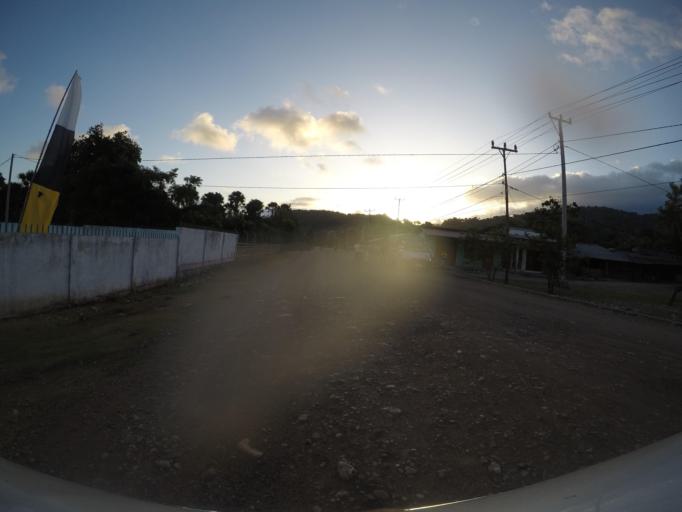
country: TL
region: Baucau
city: Venilale
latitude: -8.7499
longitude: 126.6980
